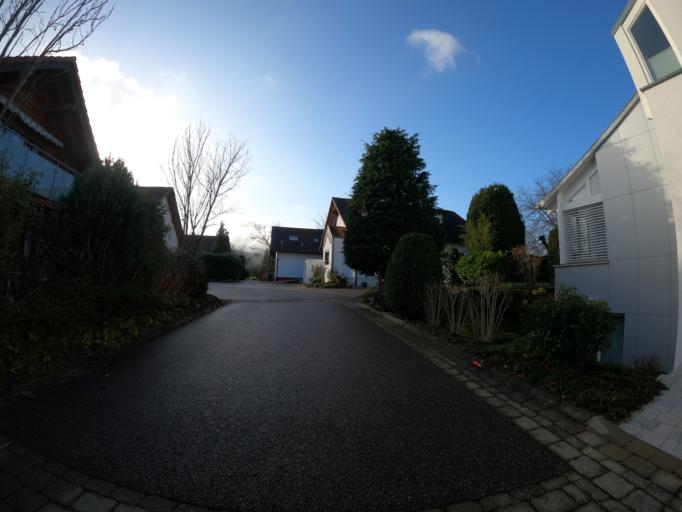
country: DE
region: Baden-Wuerttemberg
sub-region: Regierungsbezirk Stuttgart
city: Boll
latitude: 48.6459
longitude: 9.6093
